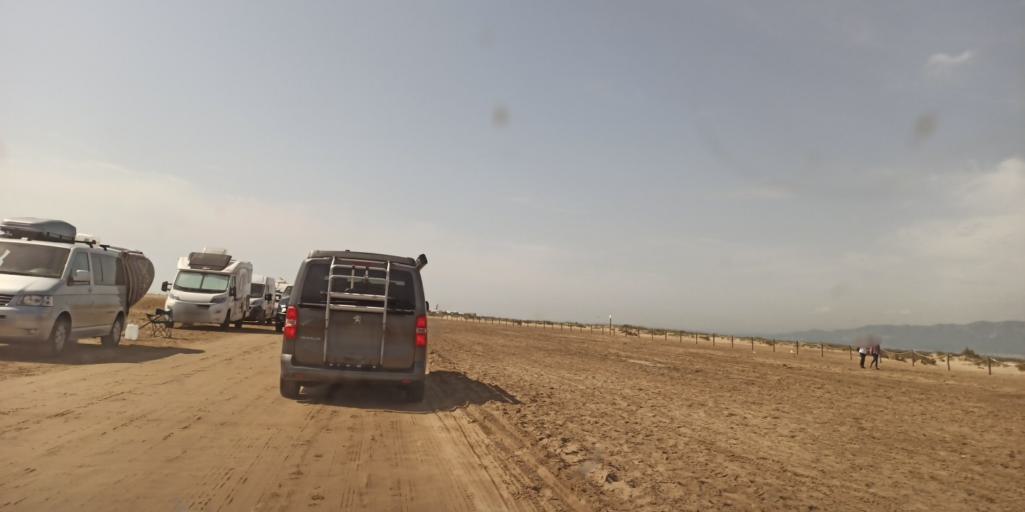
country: ES
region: Catalonia
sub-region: Provincia de Tarragona
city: Deltebre
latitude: 40.6331
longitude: 0.7459
